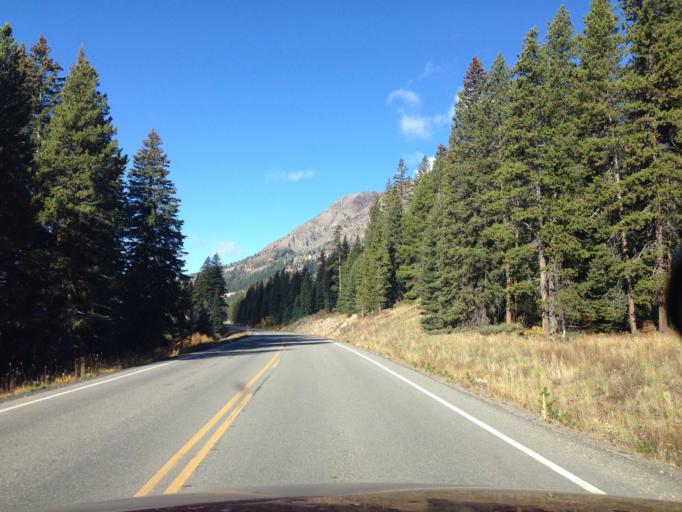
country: US
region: Montana
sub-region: Stillwater County
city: Absarokee
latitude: 45.0183
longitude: -109.9435
